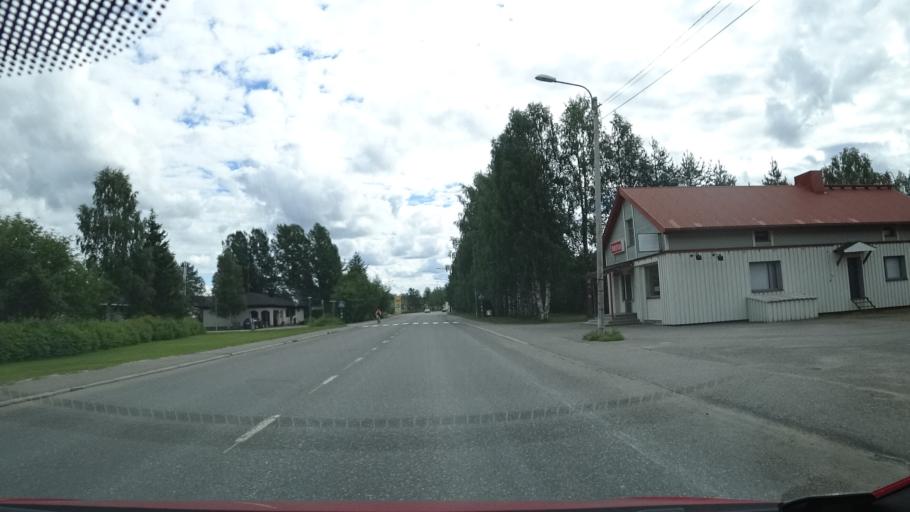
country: FI
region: Lapland
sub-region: Tunturi-Lappi
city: Kittilae
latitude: 67.6621
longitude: 24.9005
